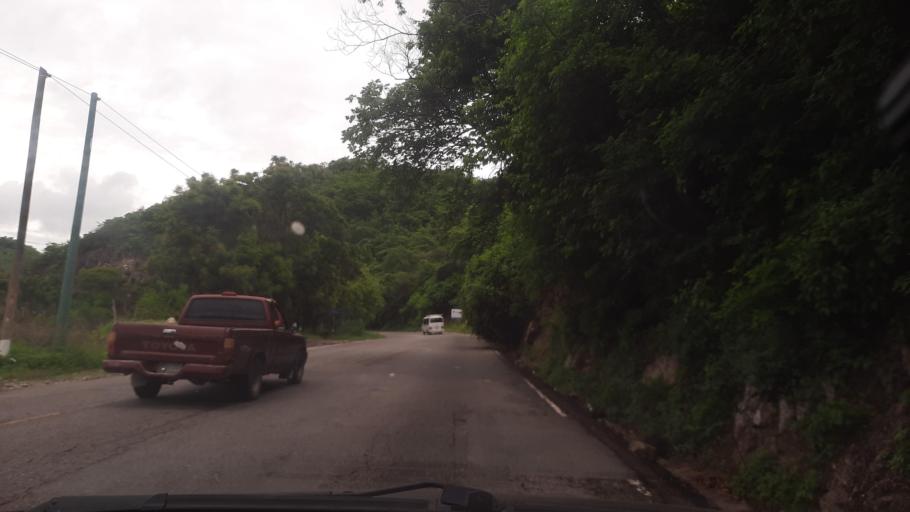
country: GT
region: Chiquimula
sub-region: Municipio de Chiquimula
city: Chiquimula
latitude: 14.8696
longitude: -89.5119
